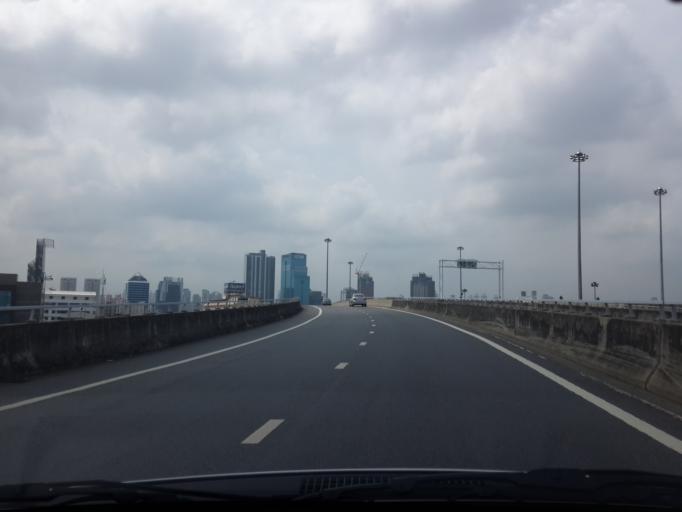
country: TH
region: Bangkok
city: Watthana
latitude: 13.7520
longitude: 100.5952
